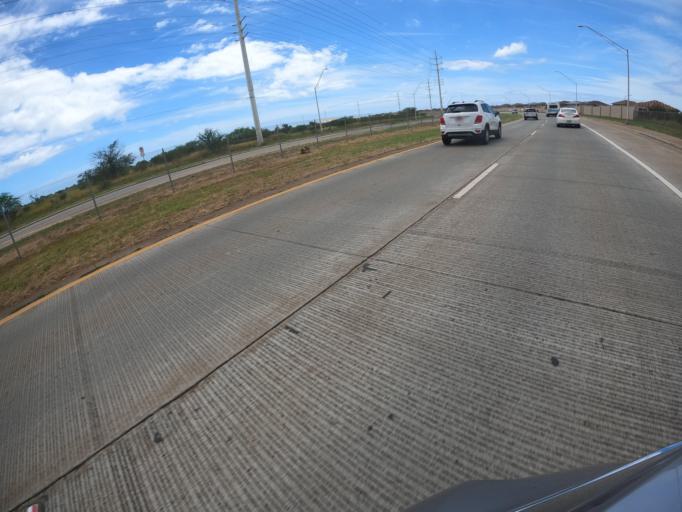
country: US
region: Hawaii
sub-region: Honolulu County
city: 'Ewa Villages
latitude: 21.3446
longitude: -158.0530
